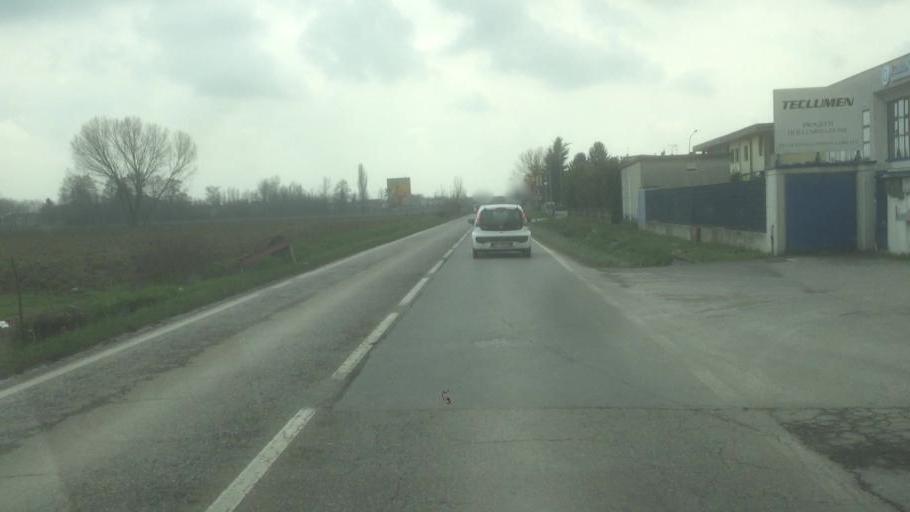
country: IT
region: Lombardy
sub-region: Provincia di Mantova
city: Casaloldo
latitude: 45.2641
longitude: 10.4773
